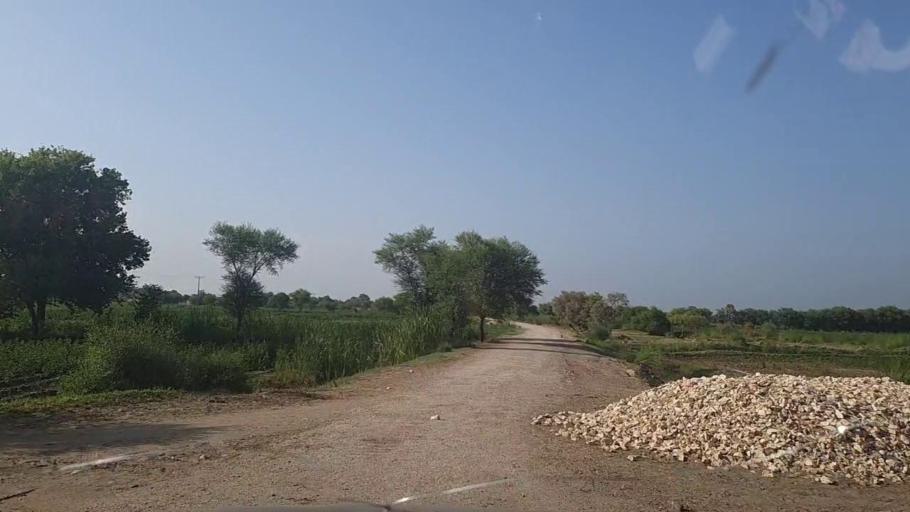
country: PK
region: Sindh
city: Khanpur
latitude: 27.7084
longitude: 69.3318
